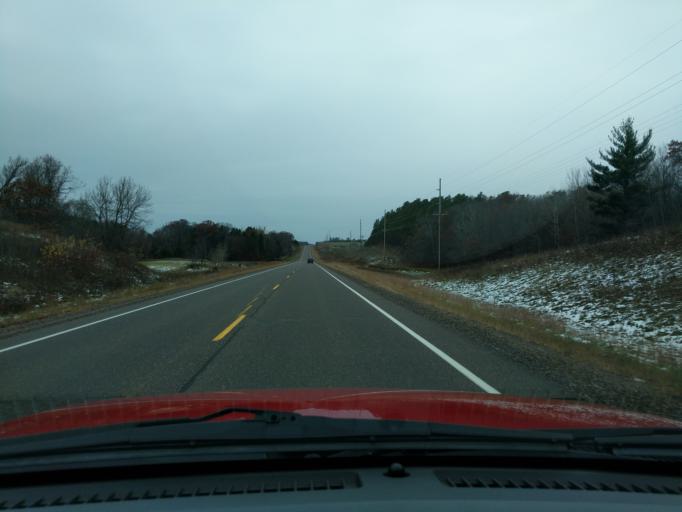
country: US
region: Wisconsin
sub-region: Washburn County
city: Shell Lake
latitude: 45.8154
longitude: -92.0604
